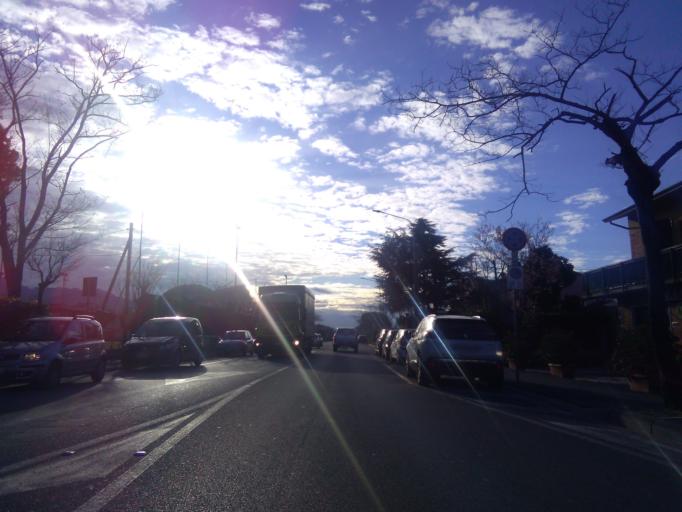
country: IT
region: Tuscany
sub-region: Provincia di Massa-Carrara
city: Marina di Carrara
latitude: 44.0523
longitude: 10.0448
